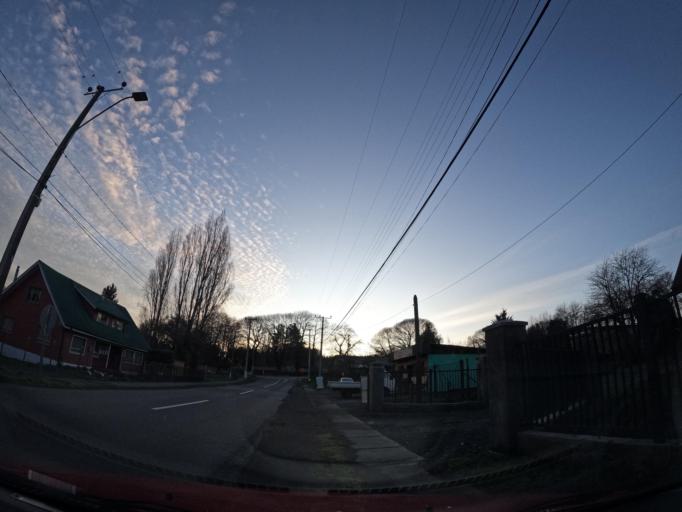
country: CL
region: Biobio
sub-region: Provincia de Biobio
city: Los Angeles
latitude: -37.4019
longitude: -72.0103
